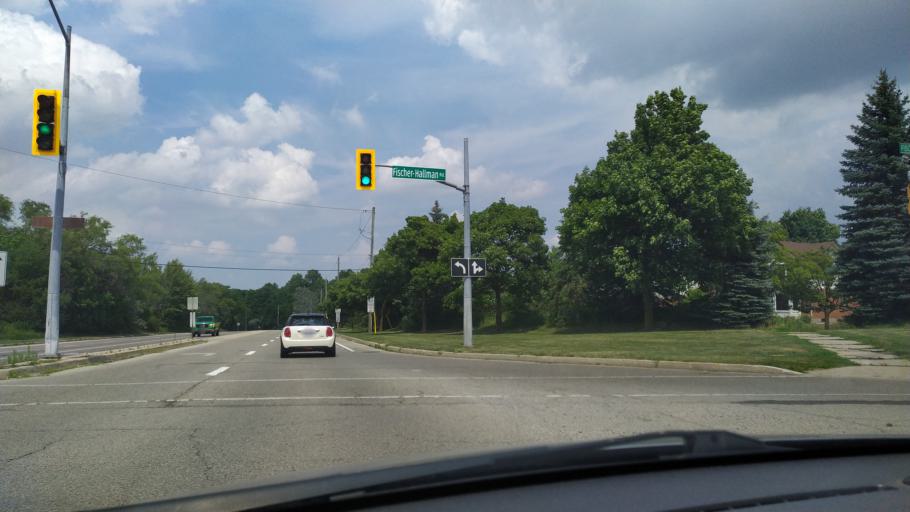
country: CA
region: Ontario
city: Waterloo
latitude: 43.4440
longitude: -80.5451
